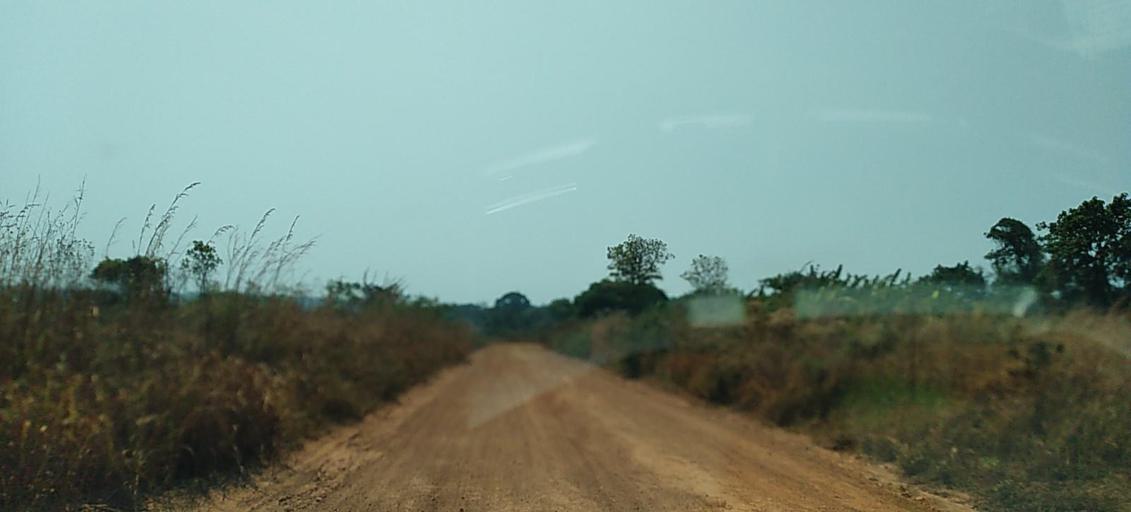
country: ZM
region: North-Western
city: Kansanshi
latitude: -12.0076
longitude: 26.5515
